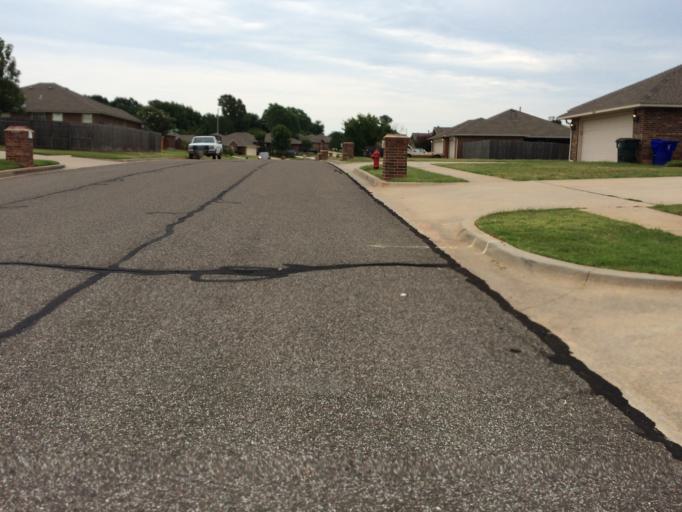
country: US
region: Oklahoma
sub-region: Cleveland County
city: Hall Park
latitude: 35.2516
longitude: -97.4224
